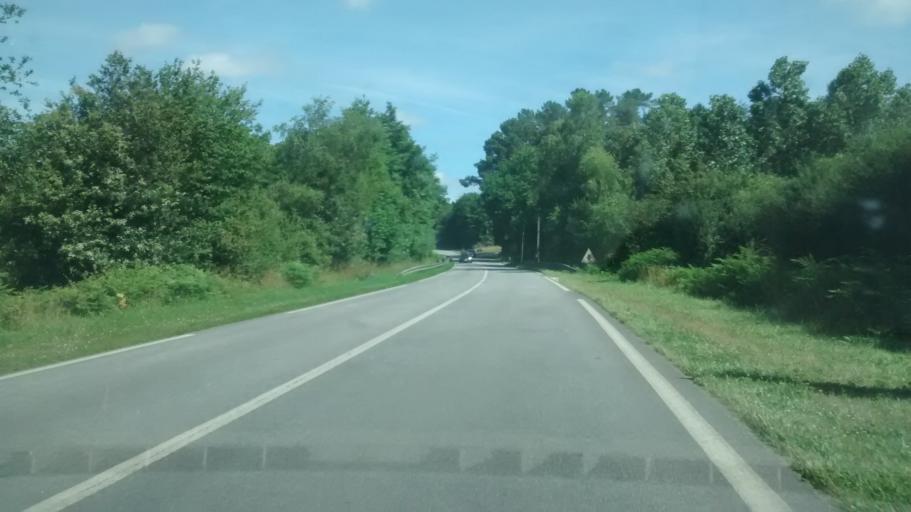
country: FR
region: Brittany
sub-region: Departement du Morbihan
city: Molac
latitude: 47.7198
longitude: -2.4390
